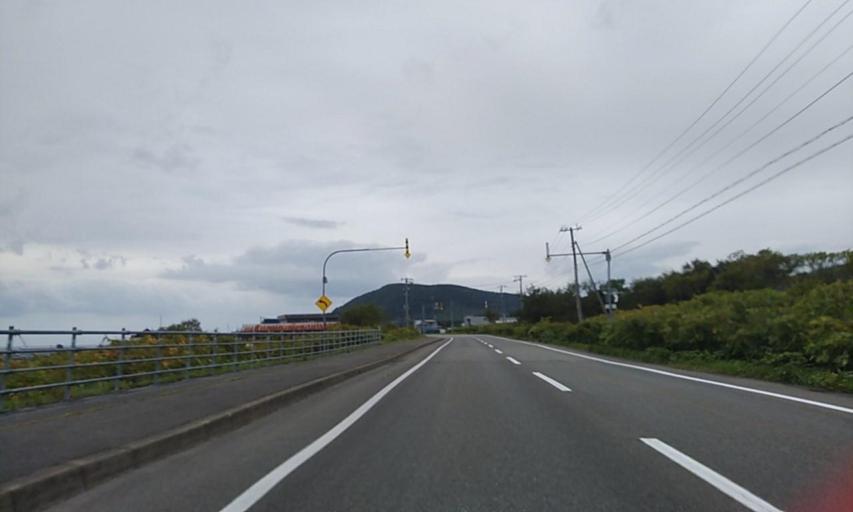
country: JP
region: Hokkaido
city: Nayoro
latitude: 45.0386
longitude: 142.5078
